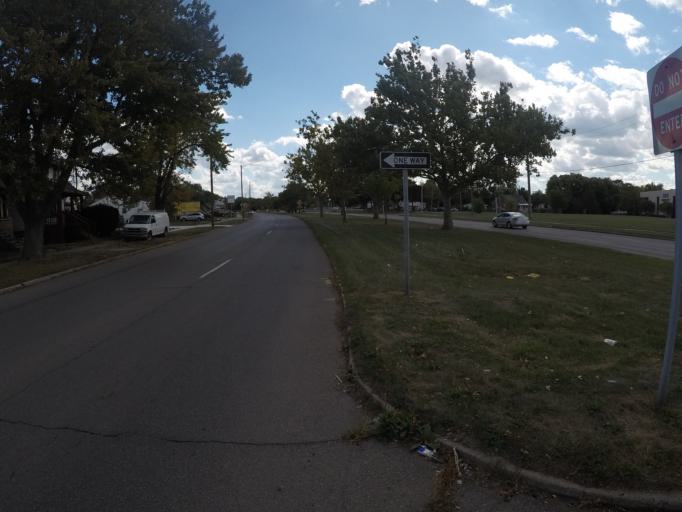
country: US
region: Michigan
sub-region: Wayne County
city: Lincoln Park
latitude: 42.2597
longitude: -83.1661
